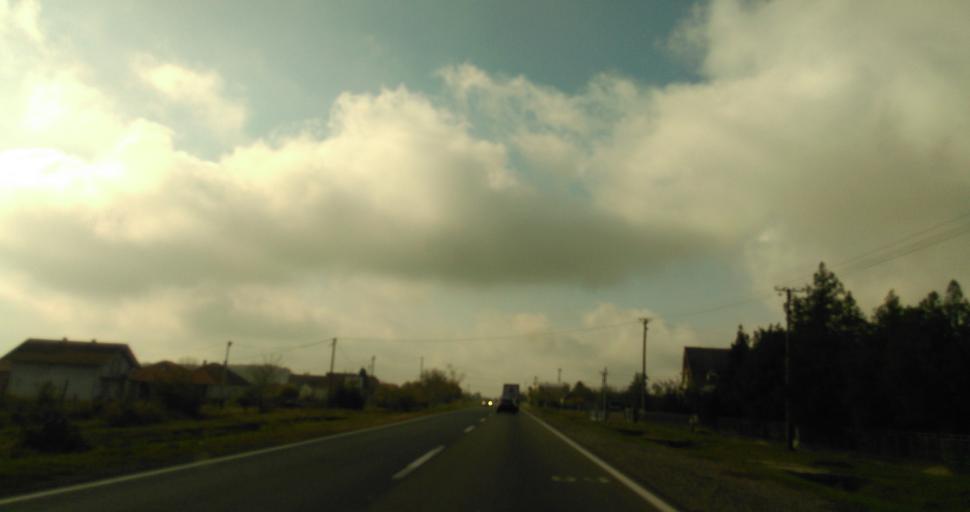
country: RS
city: Stepojevac
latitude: 44.5405
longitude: 20.2997
